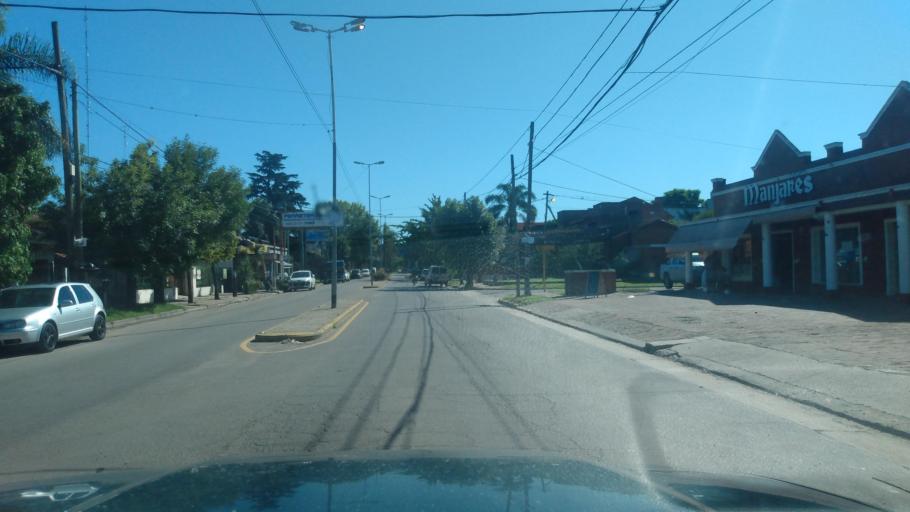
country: AR
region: Buenos Aires
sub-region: Partido de General Rodriguez
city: General Rodriguez
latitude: -34.5986
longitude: -58.9478
